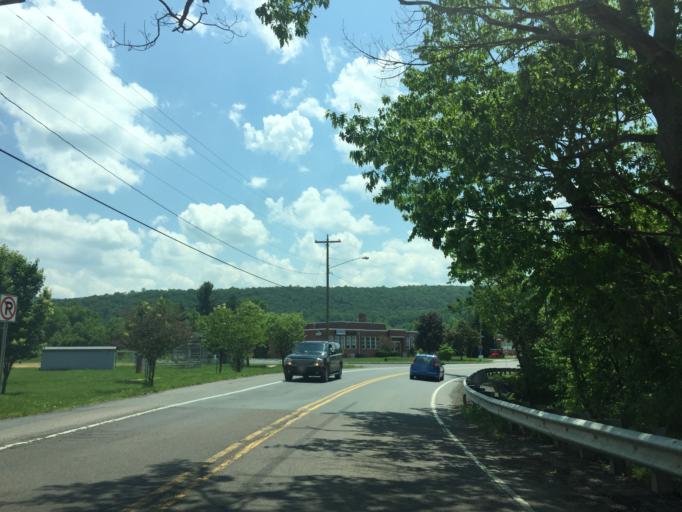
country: US
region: Virginia
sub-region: Shenandoah County
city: Woodstock
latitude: 39.0817
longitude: -78.5919
